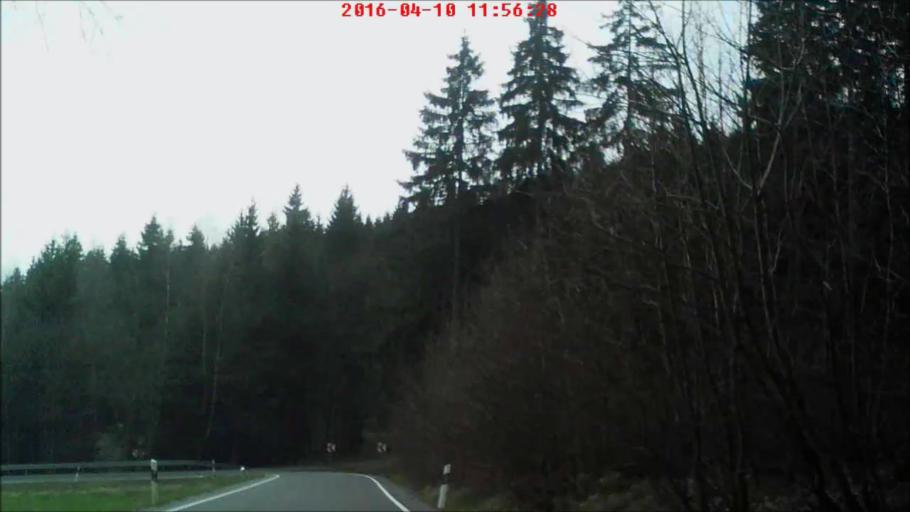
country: DE
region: Thuringia
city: Bermbach
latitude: 50.6813
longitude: 10.6427
